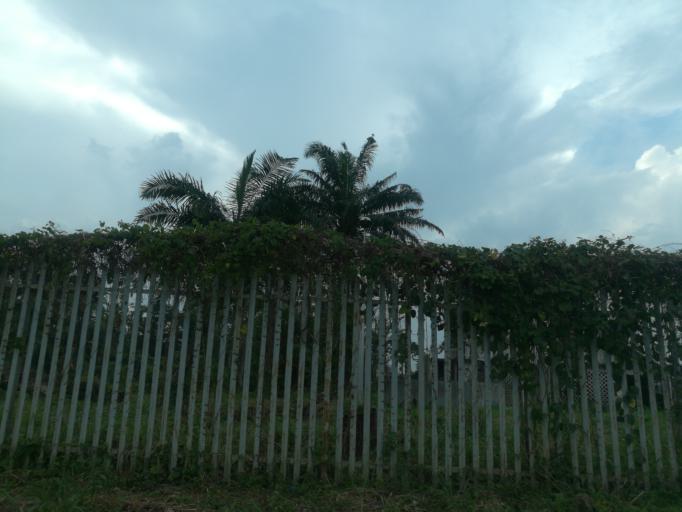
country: NG
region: Oyo
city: Ibadan
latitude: 7.4196
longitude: 3.9052
